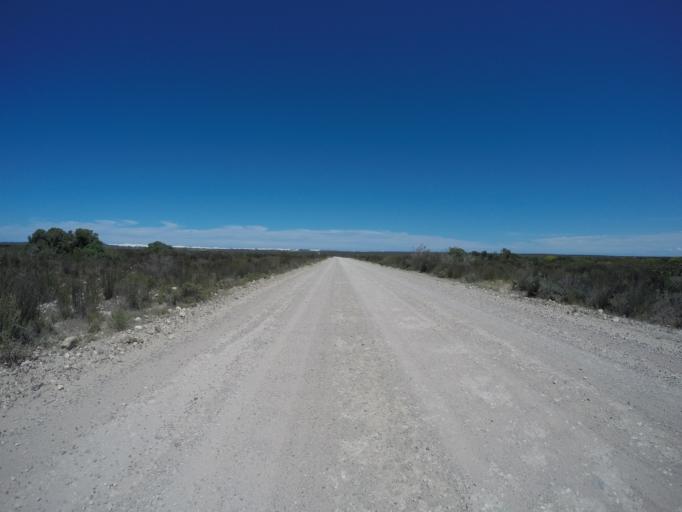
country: ZA
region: Western Cape
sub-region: Overberg District Municipality
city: Bredasdorp
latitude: -34.4438
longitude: 20.4217
